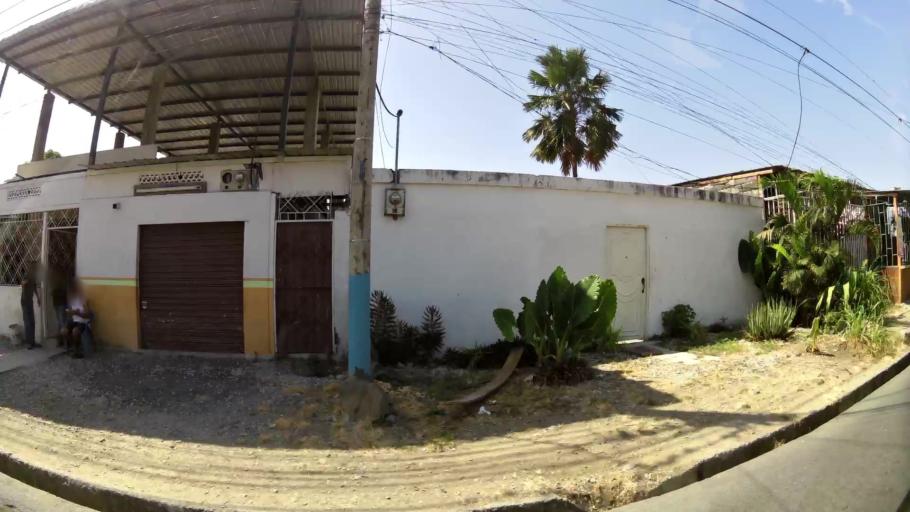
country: EC
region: Guayas
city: Eloy Alfaro
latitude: -2.1277
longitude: -79.9139
